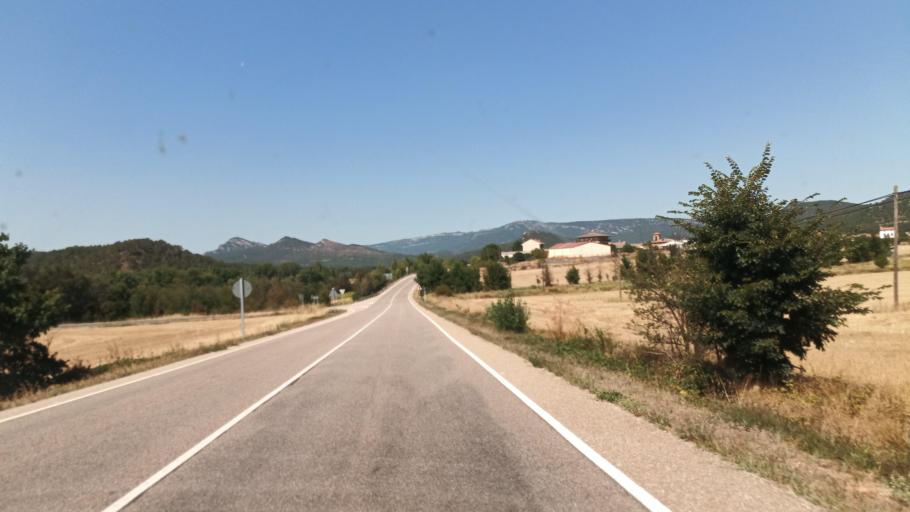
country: ES
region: Castille and Leon
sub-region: Provincia de Burgos
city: Salas de Bureba
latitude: 42.6778
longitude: -3.4247
